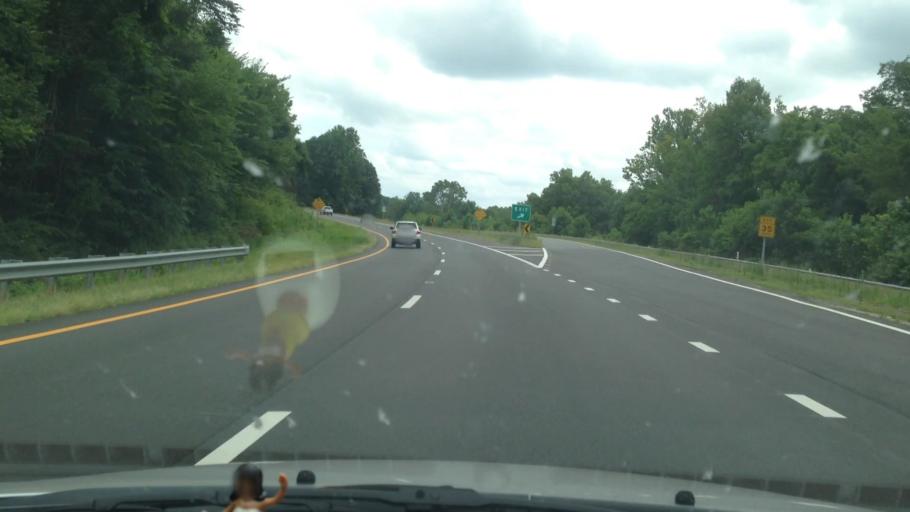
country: US
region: Virginia
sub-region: Pittsylvania County
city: Gretna
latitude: 36.9248
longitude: -79.3765
